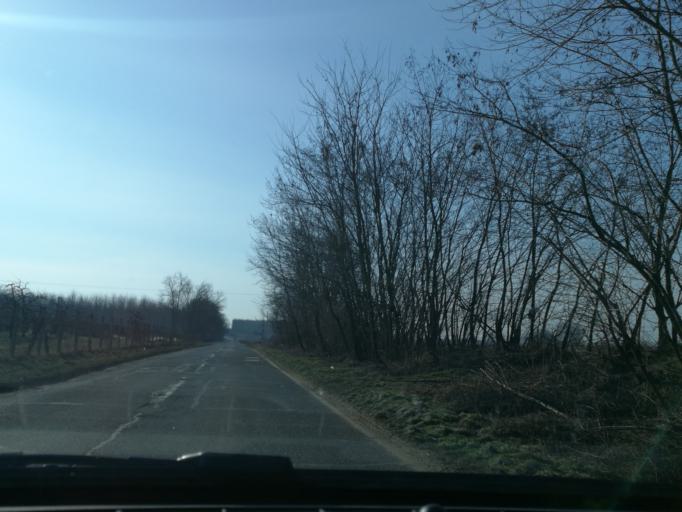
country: HU
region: Szabolcs-Szatmar-Bereg
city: Levelek
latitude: 48.0037
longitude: 21.9637
